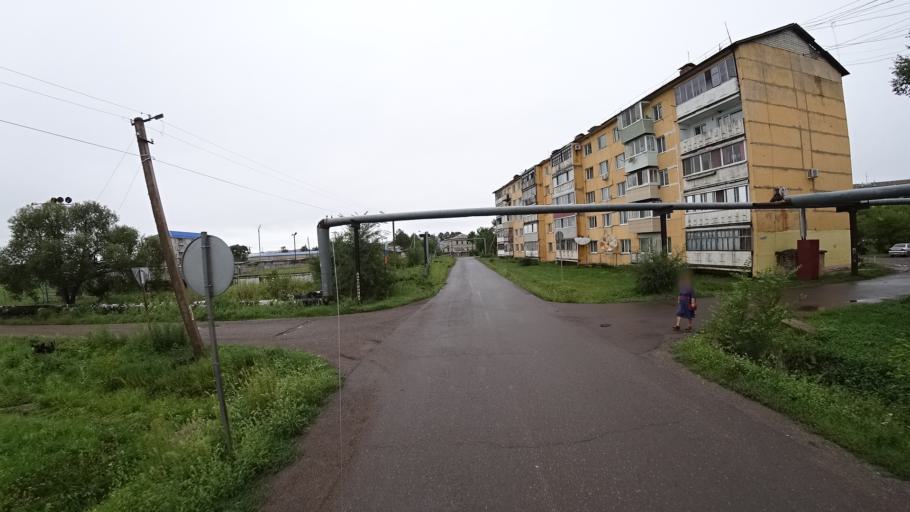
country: RU
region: Primorskiy
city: Monastyrishche
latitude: 44.2070
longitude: 132.4475
